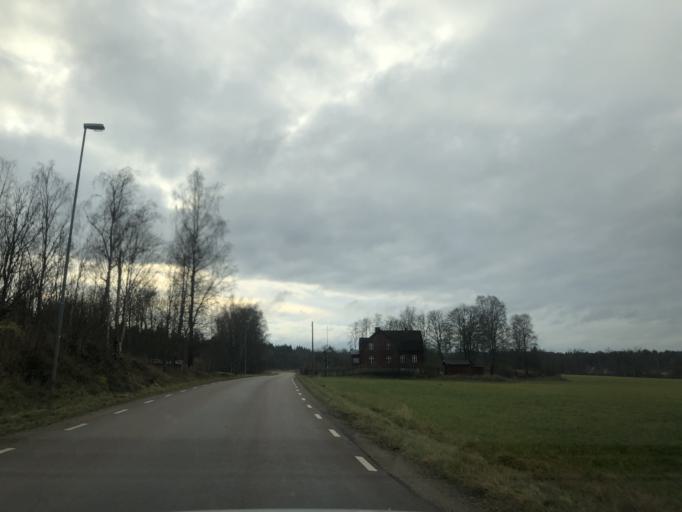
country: SE
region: Vaestra Goetaland
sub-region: Boras Kommun
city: Dalsjofors
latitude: 57.8252
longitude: 13.1581
